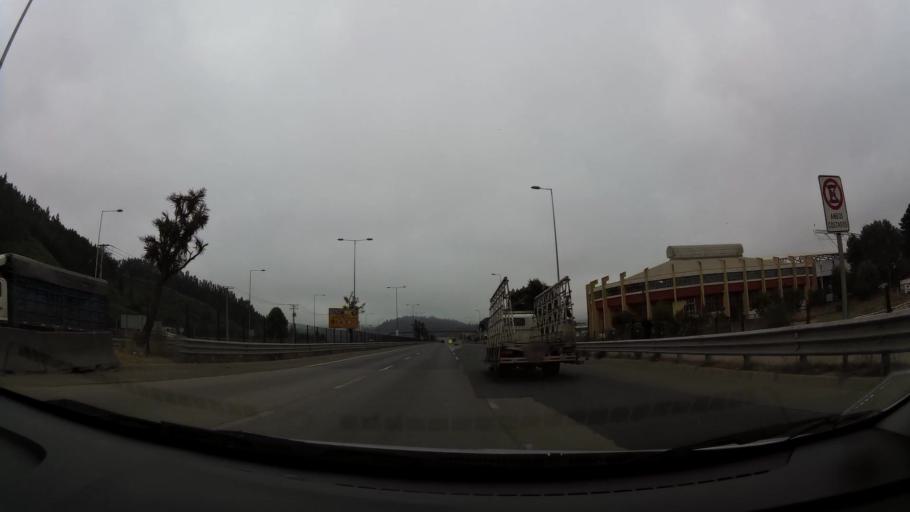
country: CL
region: Biobio
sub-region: Provincia de Concepcion
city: Concepcion
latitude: -36.8128
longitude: -73.0242
